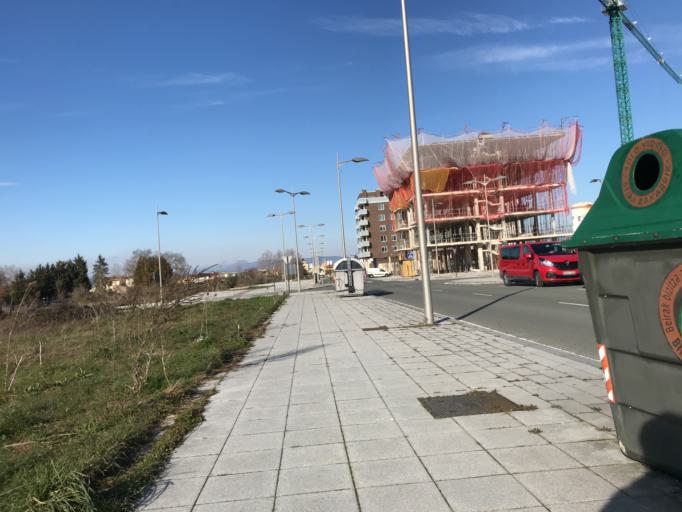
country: ES
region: Basque Country
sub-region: Provincia de Alava
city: Gasteiz / Vitoria
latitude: 42.8262
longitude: -2.6751
